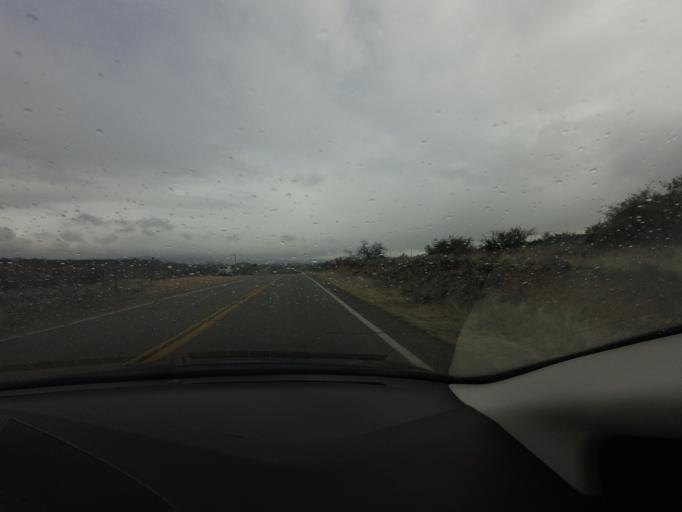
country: US
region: Arizona
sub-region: Yavapai County
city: Lake Montezuma
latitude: 34.6625
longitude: -111.8241
